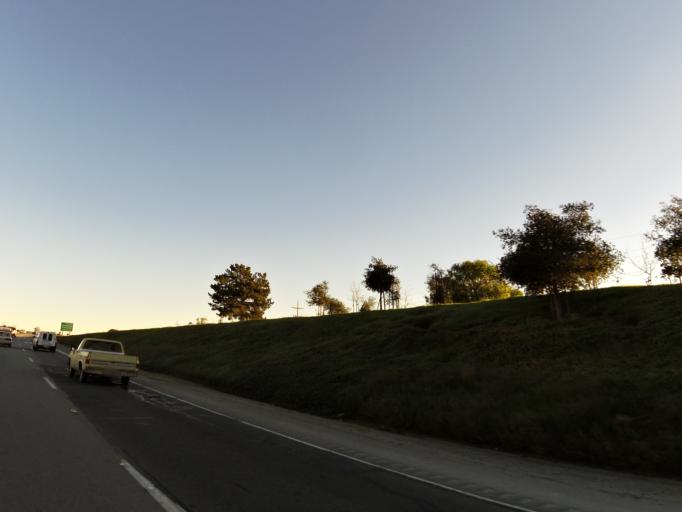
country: US
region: California
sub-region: Monterey County
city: Gonzales
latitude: 36.4646
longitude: -121.3874
